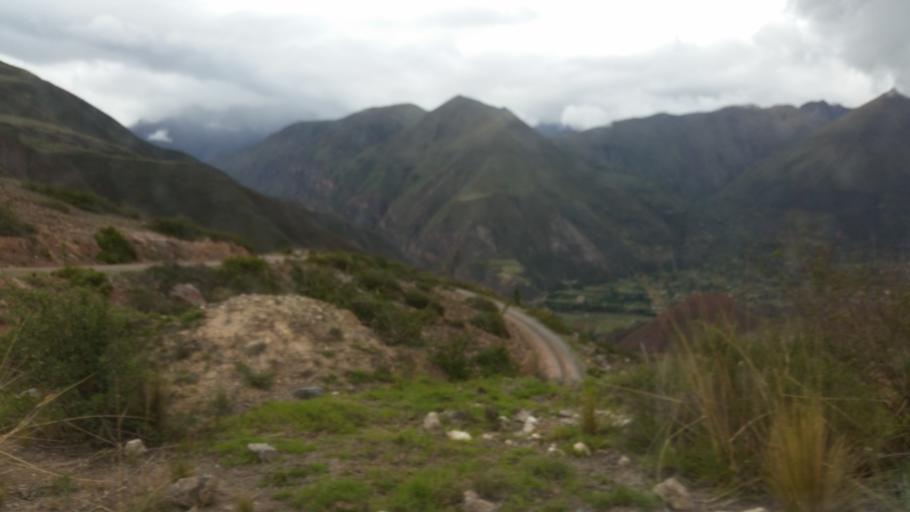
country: PE
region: Cusco
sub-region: Provincia de Urubamba
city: Maras
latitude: -13.3131
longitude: -72.1913
